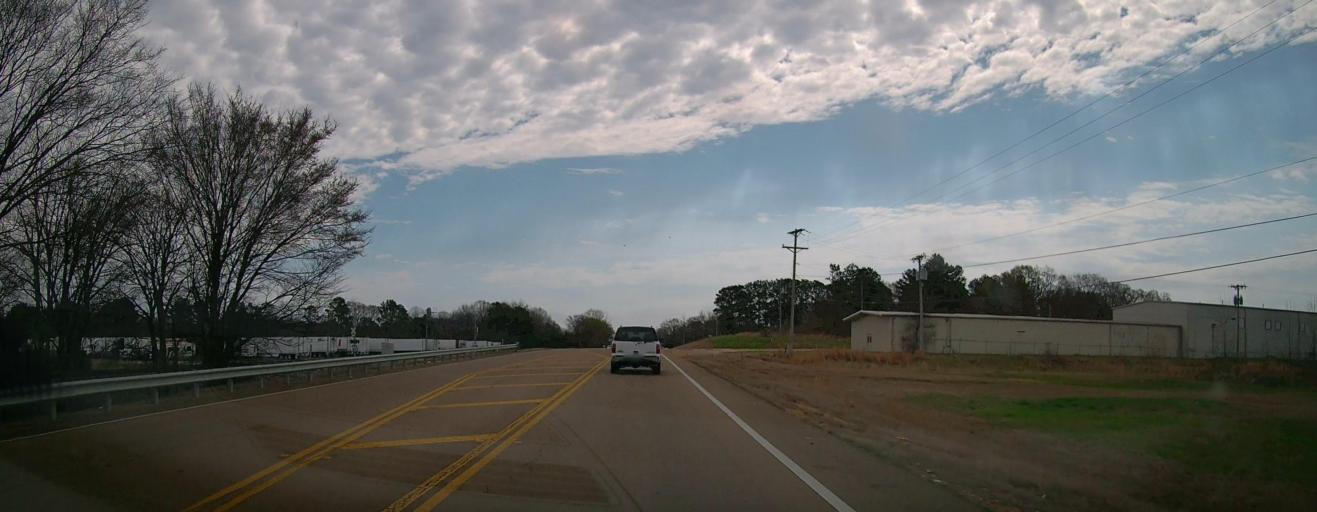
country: US
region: Mississippi
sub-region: Marshall County
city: Byhalia
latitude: 34.8830
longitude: -89.7162
